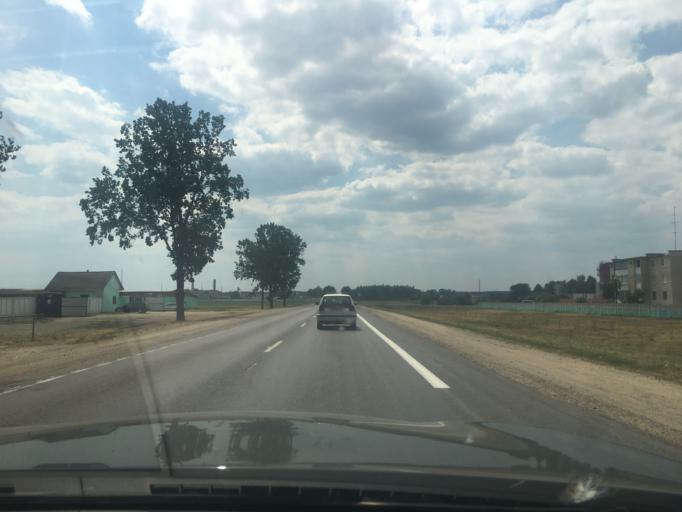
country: BY
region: Brest
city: Pruzhany
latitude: 52.5473
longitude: 24.4616
